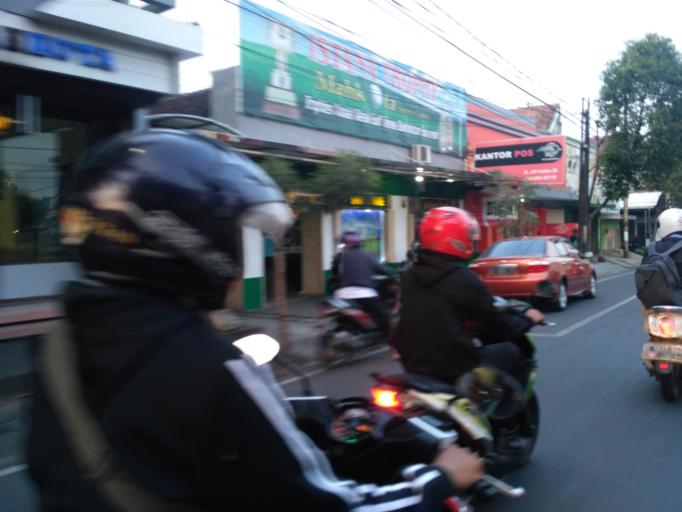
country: ID
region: East Java
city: Malang
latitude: -7.9809
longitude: 112.6279
